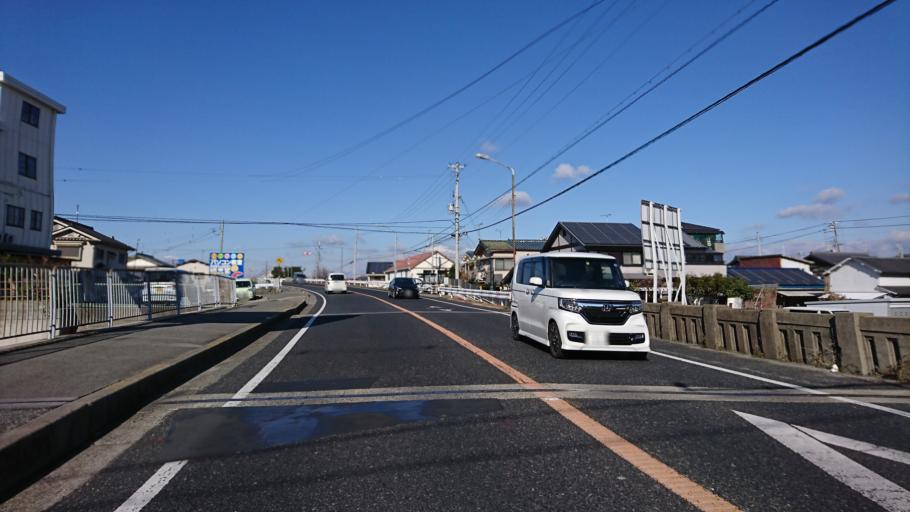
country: JP
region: Hyogo
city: Kakogawacho-honmachi
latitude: 34.7267
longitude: 134.8867
